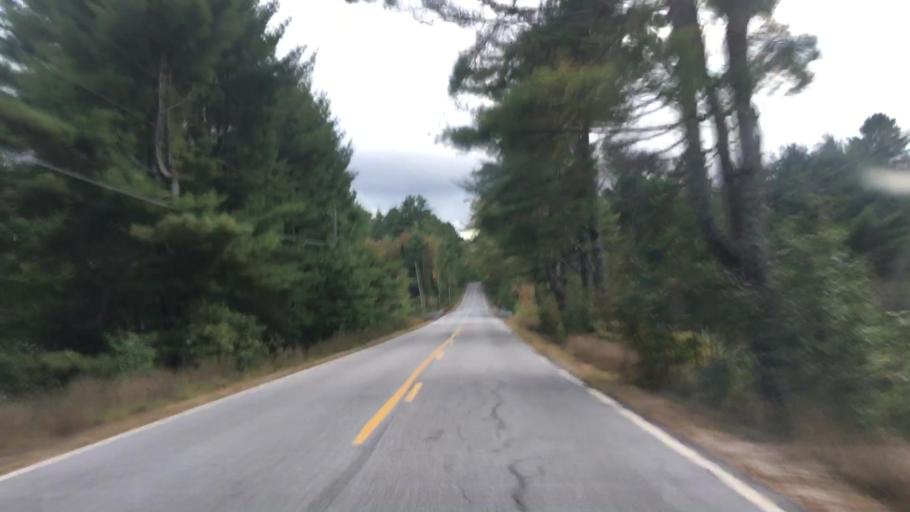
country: US
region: New Hampshire
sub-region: Carroll County
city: Effingham
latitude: 43.7072
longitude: -70.9820
